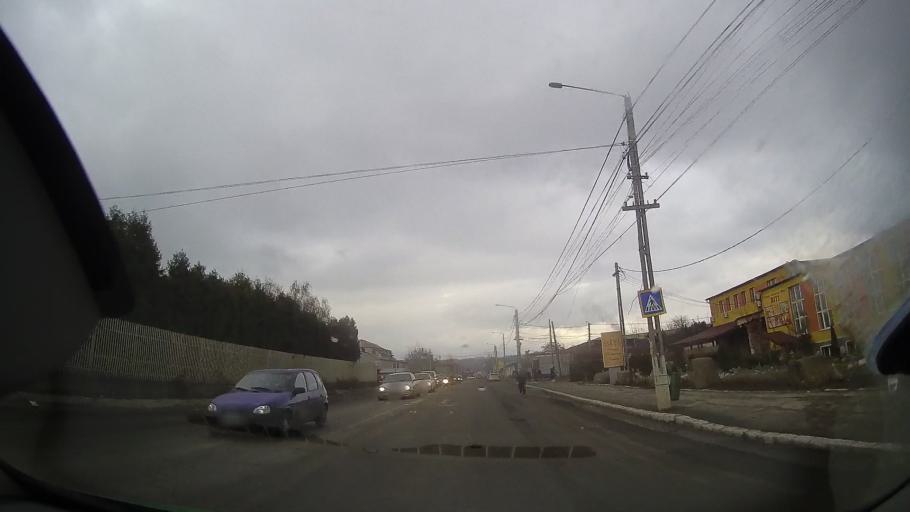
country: RO
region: Cluj
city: Turda
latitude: 46.5560
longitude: 23.7848
